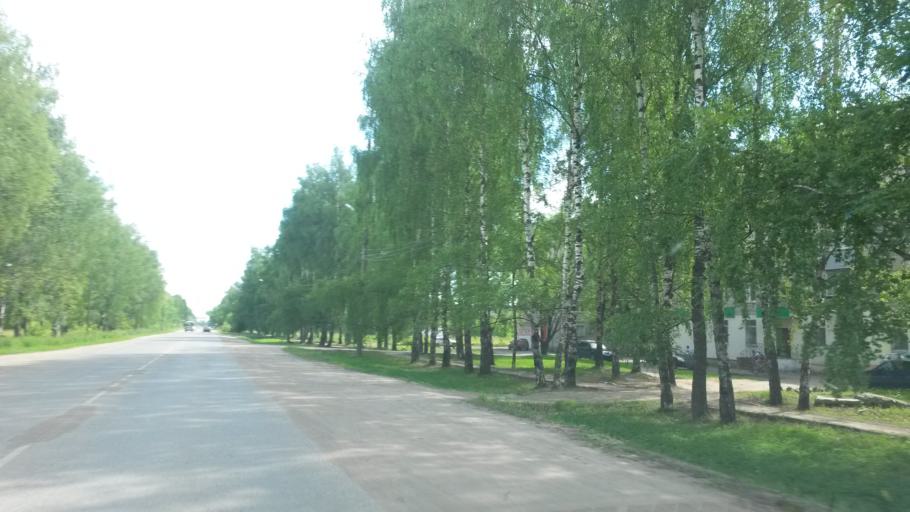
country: RU
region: Ivanovo
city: Zavolzhsk
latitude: 57.4780
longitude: 42.1514
